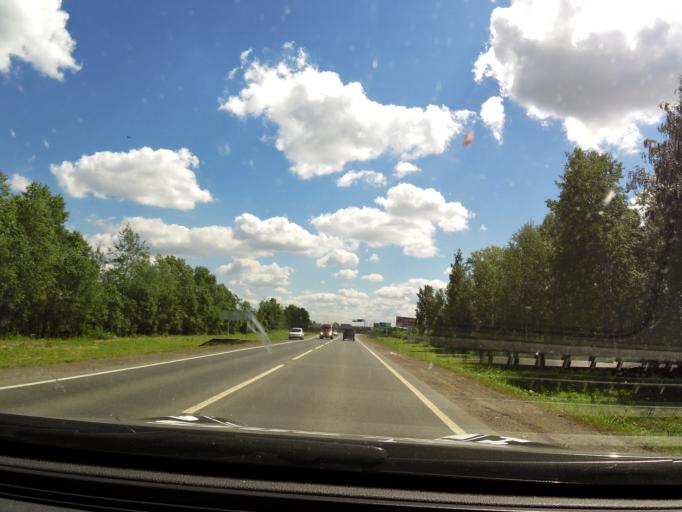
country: RU
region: Vologda
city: Molochnoye
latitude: 59.2522
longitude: 39.7659
